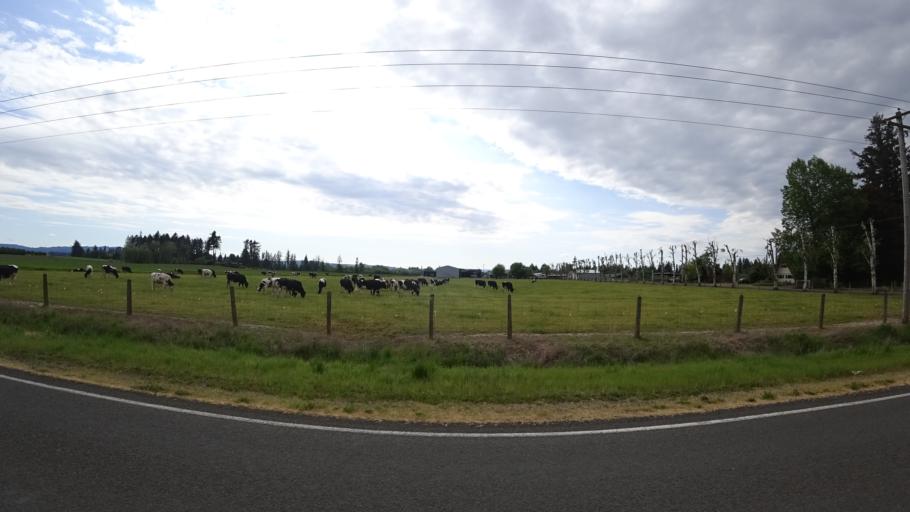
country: US
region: Oregon
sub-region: Washington County
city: Hillsboro
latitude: 45.4844
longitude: -122.9496
